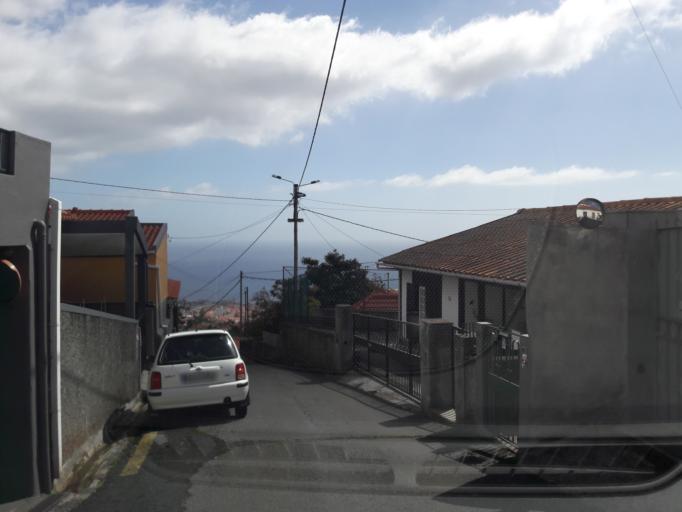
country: PT
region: Madeira
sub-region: Funchal
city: Nossa Senhora do Monte
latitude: 32.6649
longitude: -16.9134
